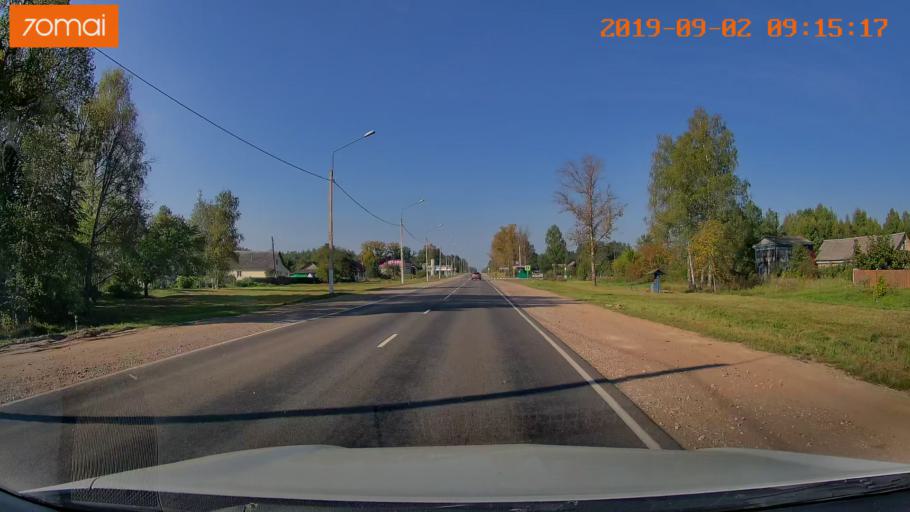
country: RU
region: Kaluga
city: Nikola-Lenivets
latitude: 54.8397
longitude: 35.4959
